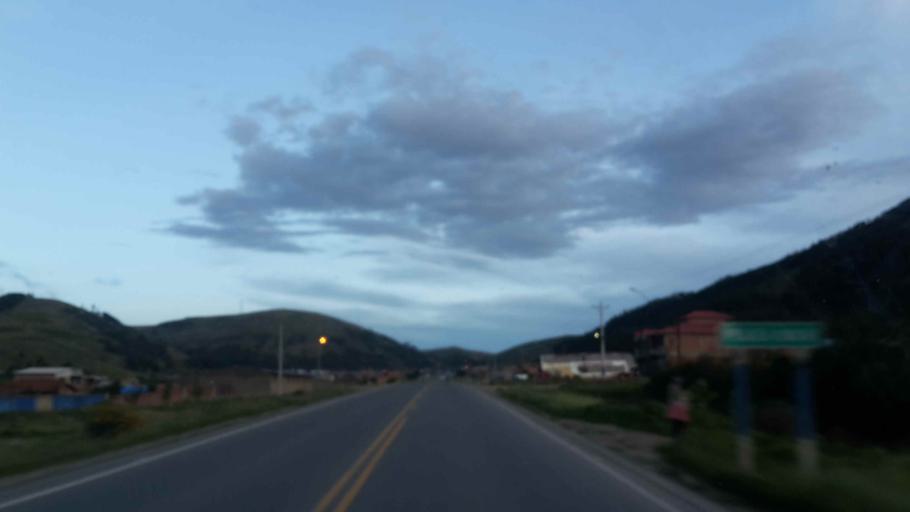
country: BO
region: Cochabamba
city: Colomi
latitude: -17.3600
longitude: -65.8448
